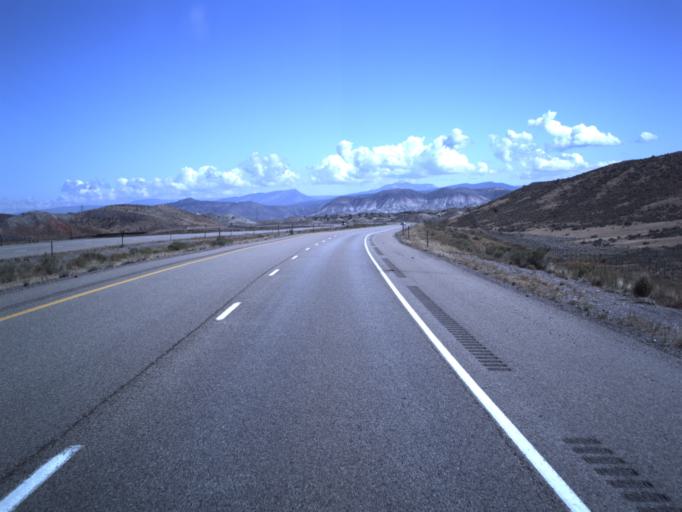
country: US
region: Utah
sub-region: Sevier County
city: Aurora
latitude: 38.8862
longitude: -111.9161
